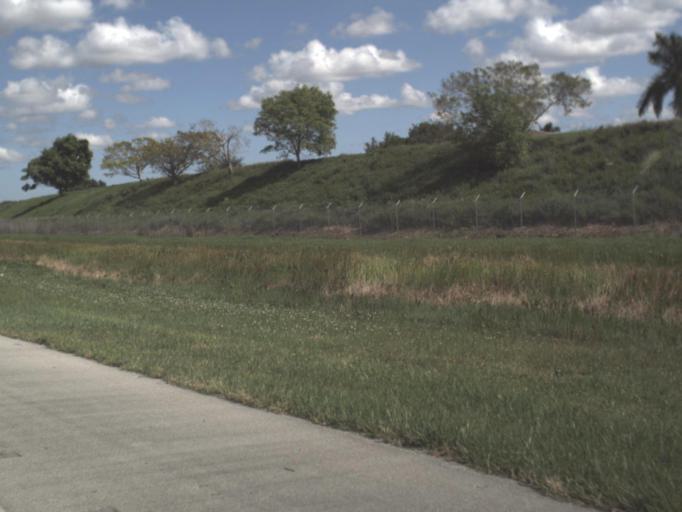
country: US
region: Florida
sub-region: Broward County
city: Coral Springs
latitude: 26.2991
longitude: -80.2953
